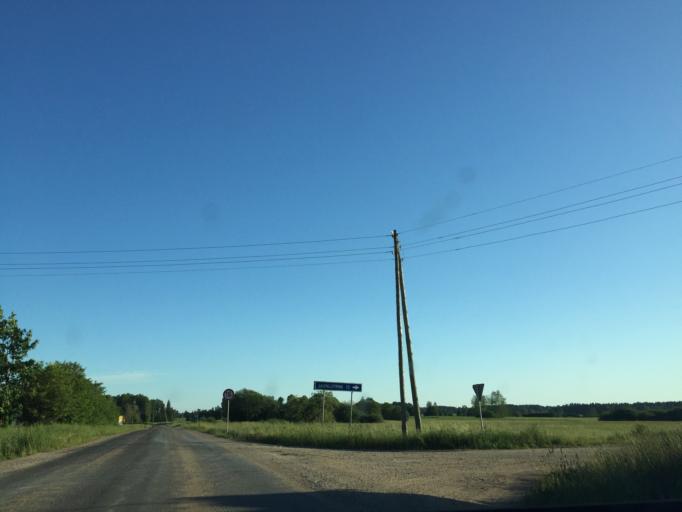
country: LV
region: Broceni
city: Broceni
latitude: 56.7728
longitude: 22.5361
